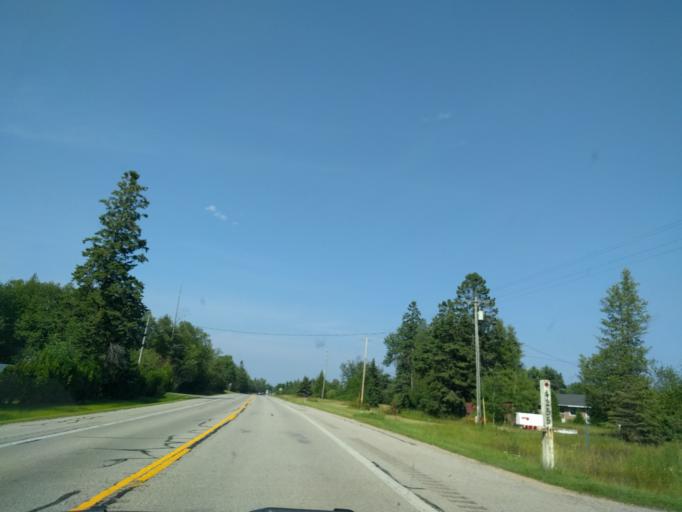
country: US
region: Michigan
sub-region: Delta County
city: Escanaba
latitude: 45.6711
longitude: -87.1532
